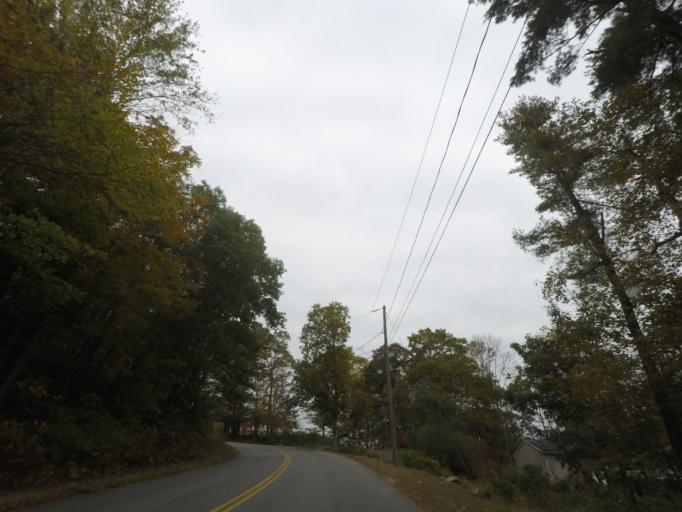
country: US
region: Connecticut
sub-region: Windham County
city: Thompson
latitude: 41.9474
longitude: -71.8366
